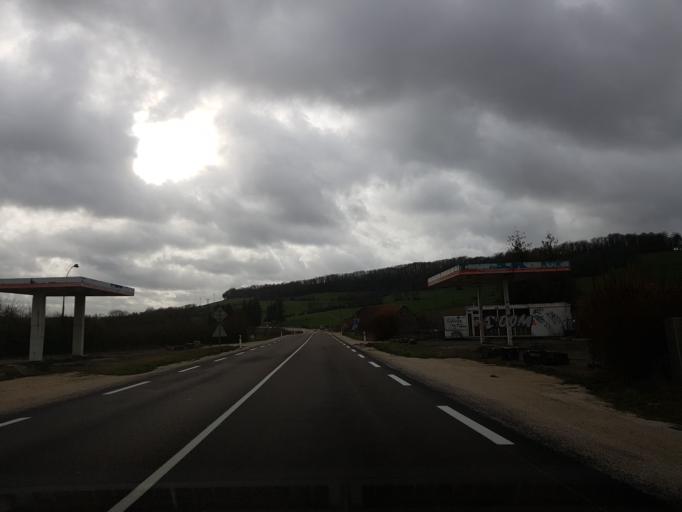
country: FR
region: Champagne-Ardenne
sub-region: Departement de la Haute-Marne
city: Rolampont
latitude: 47.9194
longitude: 5.2913
